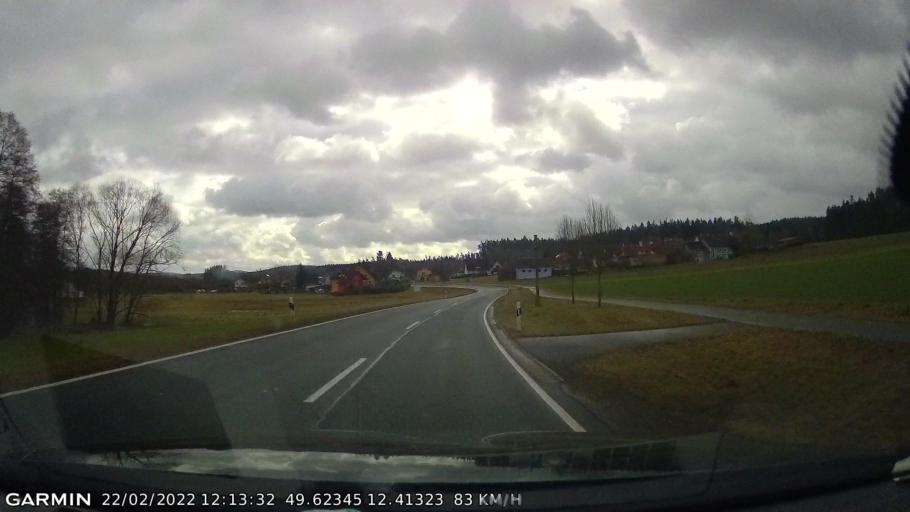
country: DE
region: Bavaria
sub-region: Upper Palatinate
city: Pleystein
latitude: 49.6231
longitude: 12.4132
